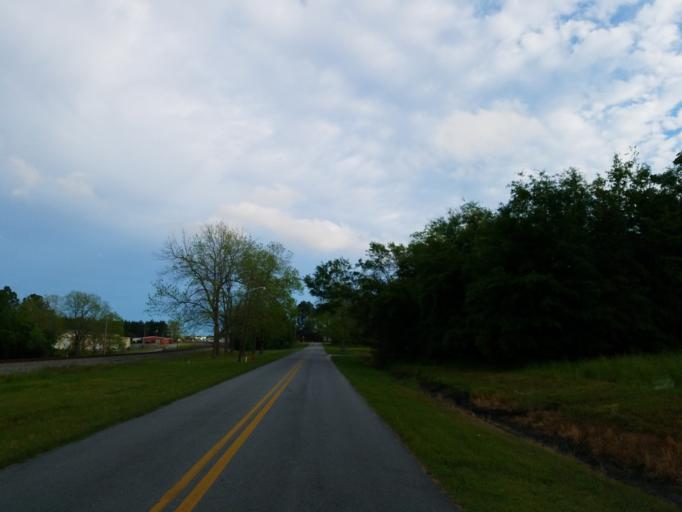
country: US
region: Georgia
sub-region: Crisp County
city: Cordele
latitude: 31.8307
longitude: -83.7394
